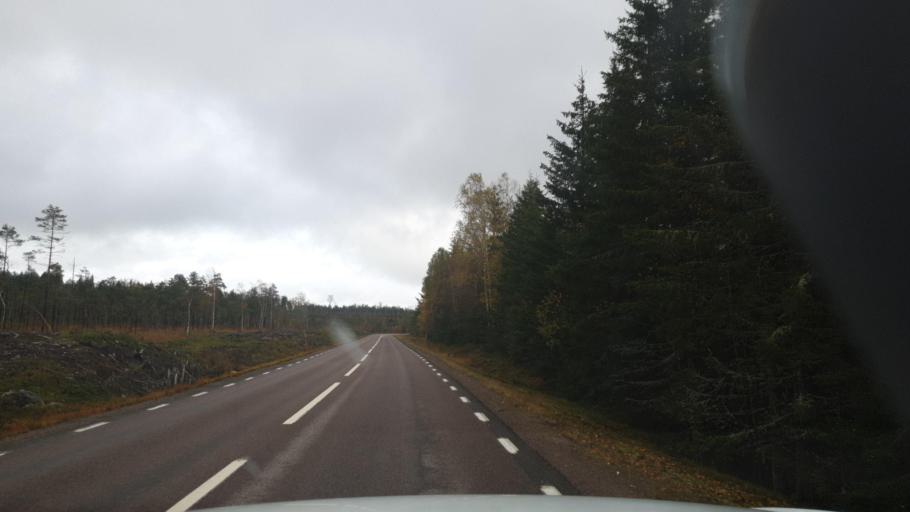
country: SE
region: Vaermland
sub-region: Sunne Kommun
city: Sunne
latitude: 59.6916
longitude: 13.0662
